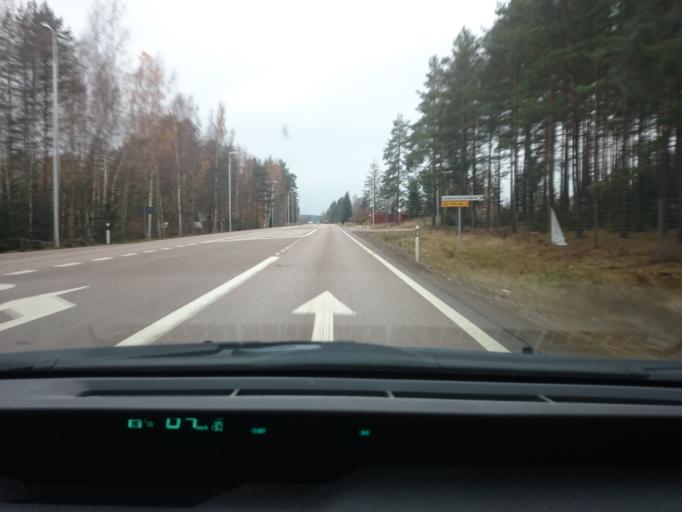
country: SE
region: Dalarna
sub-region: Avesta Kommun
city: Avesta
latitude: 60.1814
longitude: 16.1306
